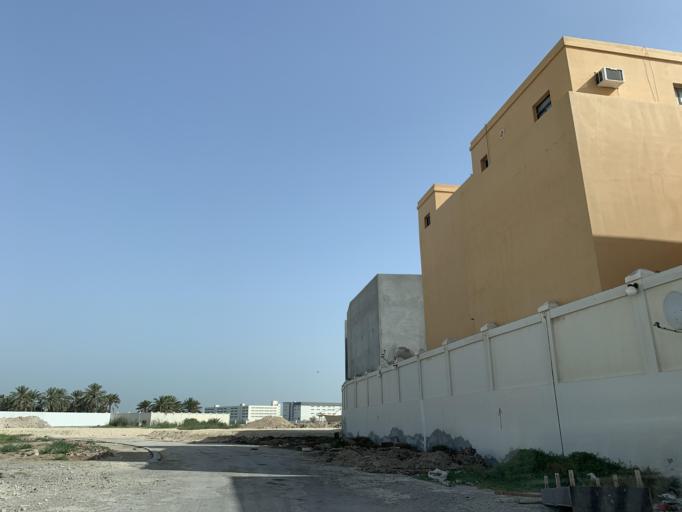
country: BH
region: Northern
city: Sitrah
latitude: 26.1471
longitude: 50.6110
